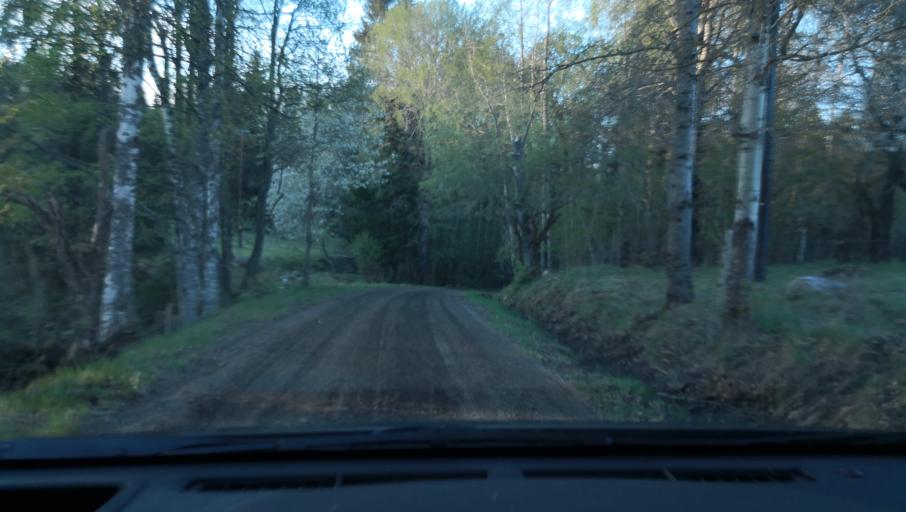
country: SE
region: OErebro
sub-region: Askersunds Kommun
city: Asbro
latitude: 58.8729
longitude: 15.1438
